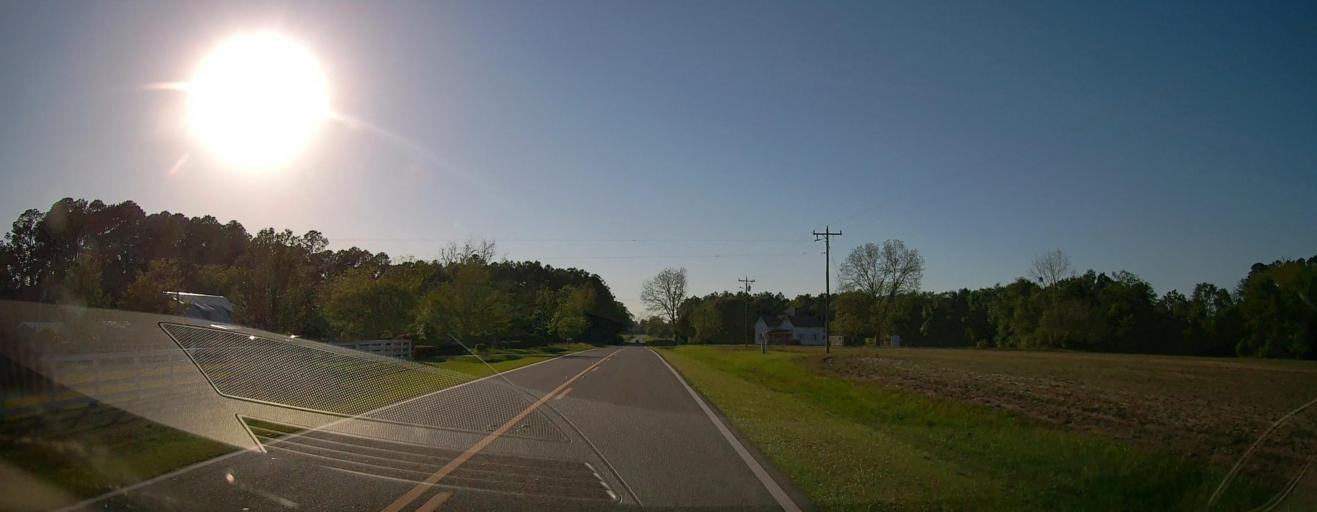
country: US
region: Georgia
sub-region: Ben Hill County
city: Fitzgerald
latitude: 31.6791
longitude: -83.1970
